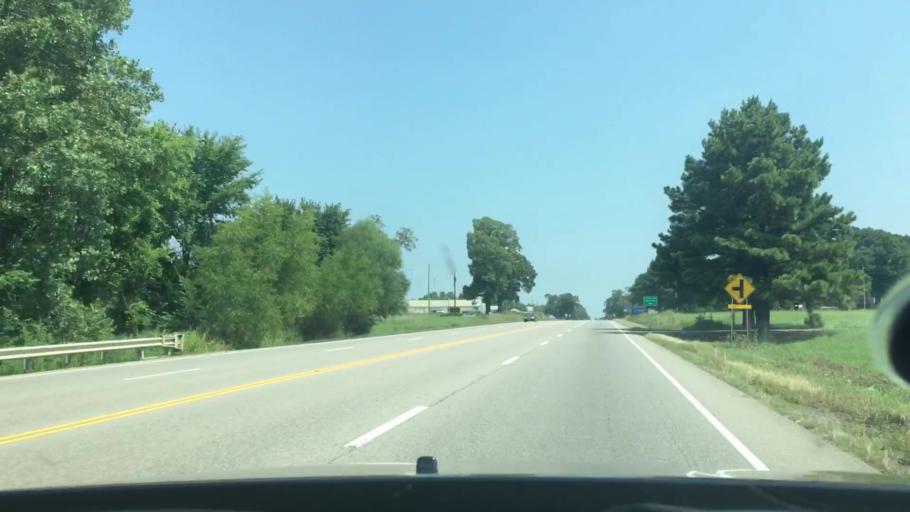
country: US
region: Oklahoma
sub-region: Atoka County
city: Atoka
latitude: 34.3297
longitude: -96.1616
